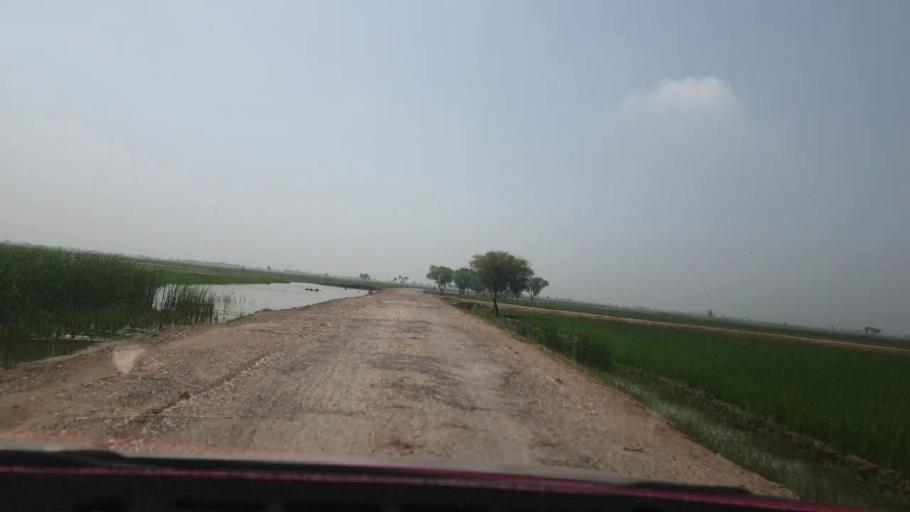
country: PK
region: Sindh
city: Nasirabad
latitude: 27.3993
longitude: 67.8493
